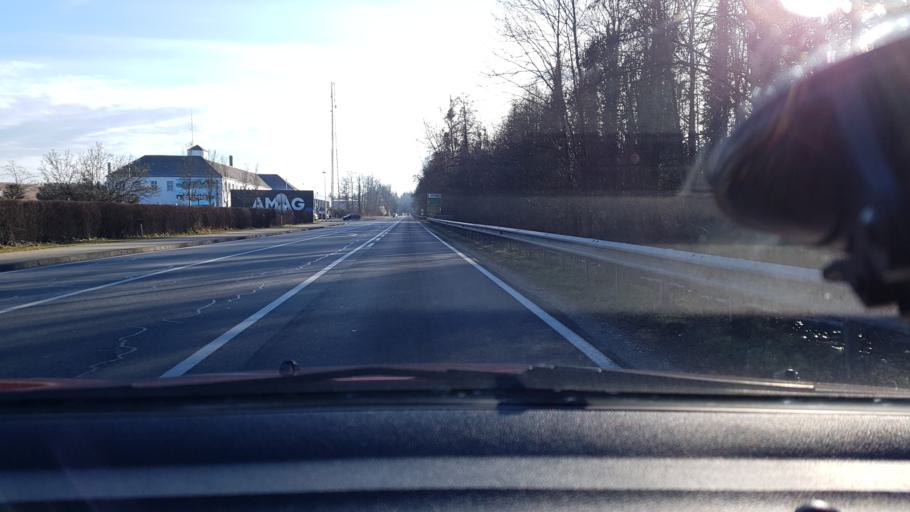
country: AT
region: Upper Austria
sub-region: Politischer Bezirk Braunau am Inn
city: Braunau am Inn
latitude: 48.2248
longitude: 13.0263
